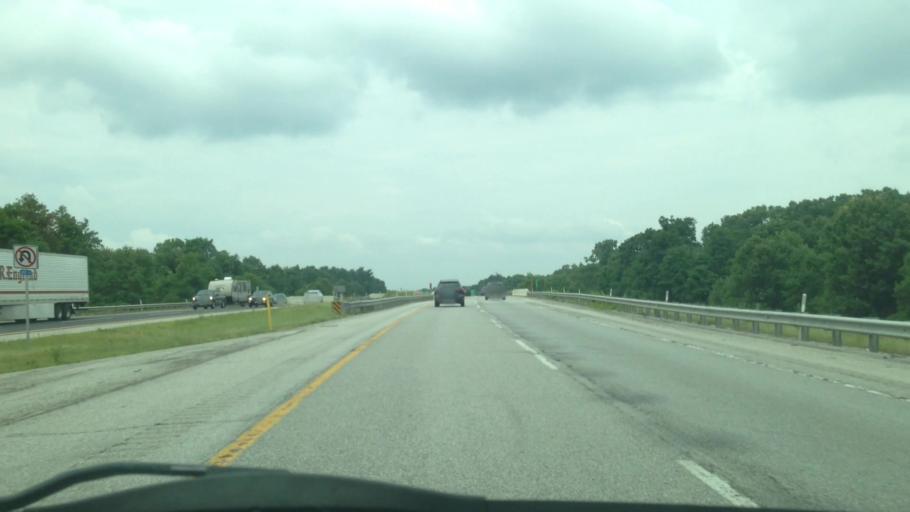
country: US
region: Indiana
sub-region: Elkhart County
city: Bristol
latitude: 41.7305
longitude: -85.7755
